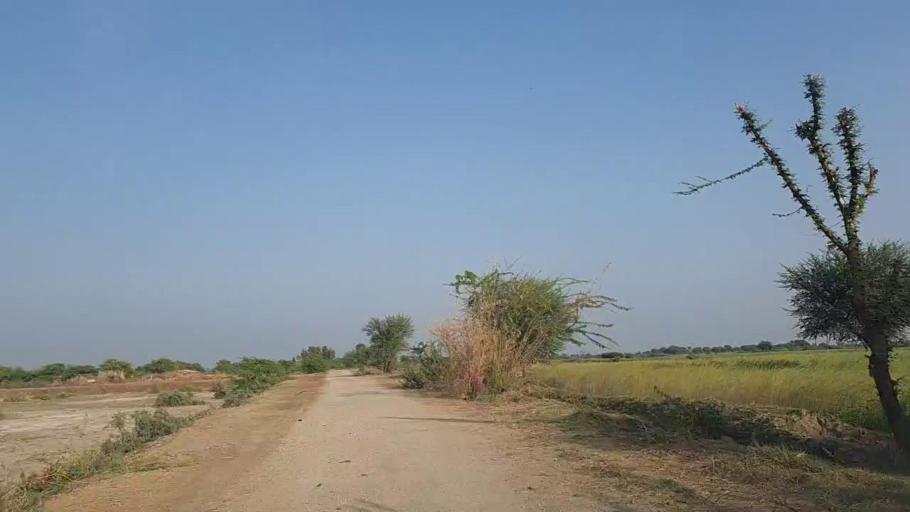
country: PK
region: Sindh
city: Dhoro Naro
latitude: 25.4920
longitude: 69.4971
